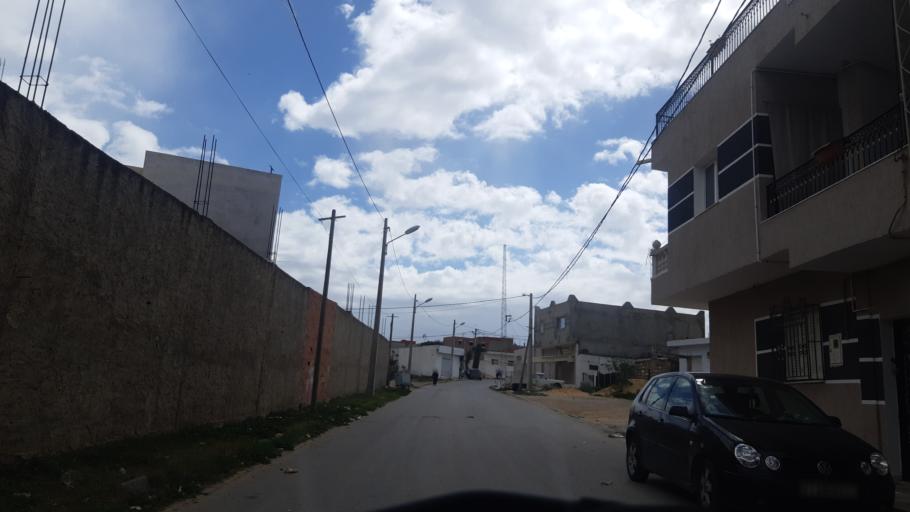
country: TN
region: Susah
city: Akouda
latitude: 35.8654
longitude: 10.5414
